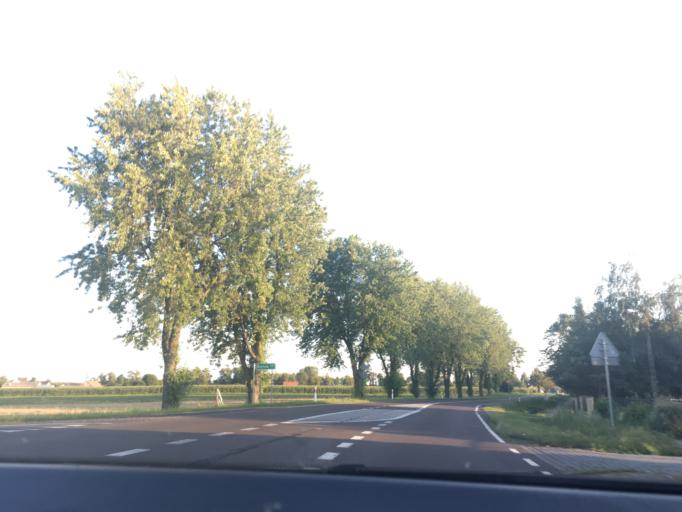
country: PL
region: Lublin Voivodeship
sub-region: Powiat radzynski
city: Radzyn Podlaski
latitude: 51.8484
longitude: 22.6987
